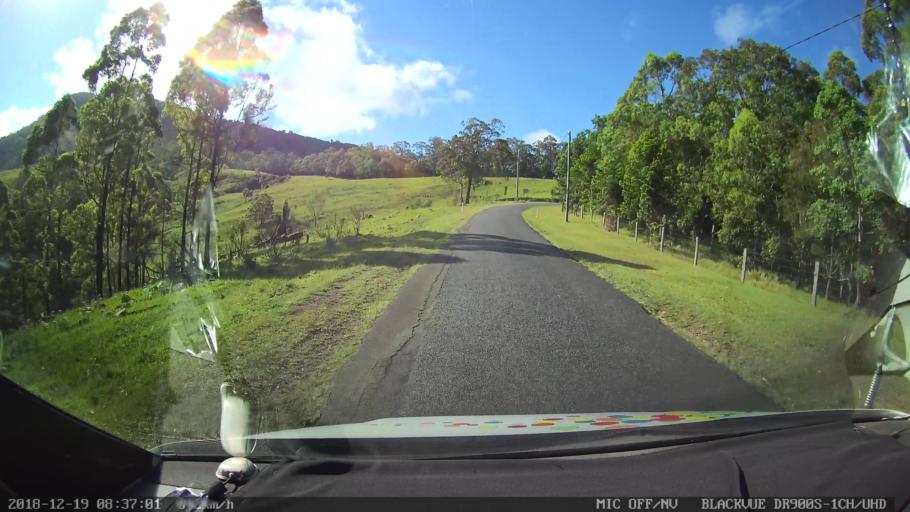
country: AU
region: New South Wales
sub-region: Kyogle
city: Kyogle
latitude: -28.3295
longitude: 152.9733
